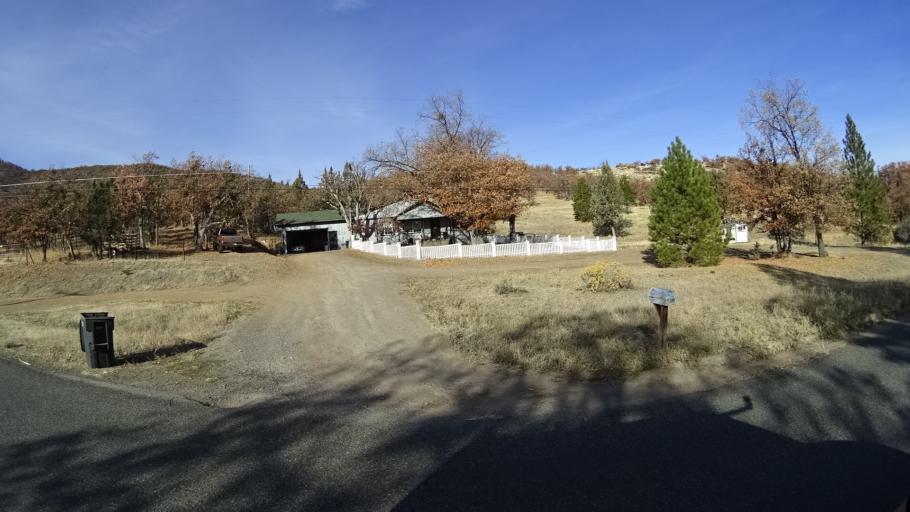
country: US
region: California
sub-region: Siskiyou County
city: Yreka
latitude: 41.6607
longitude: -122.6245
